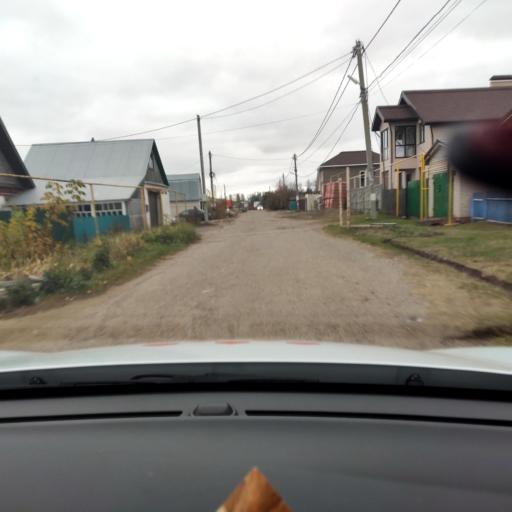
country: RU
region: Tatarstan
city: Vysokaya Gora
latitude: 55.8730
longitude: 49.2511
